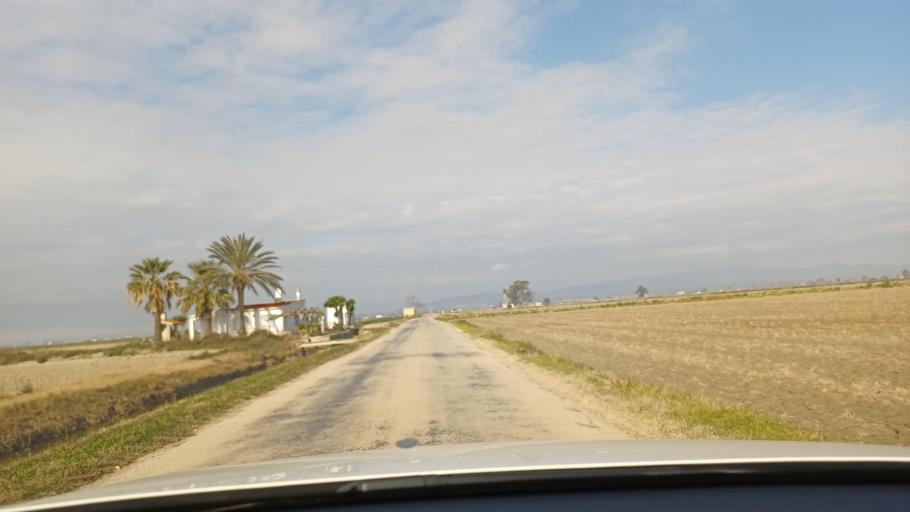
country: ES
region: Catalonia
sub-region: Provincia de Tarragona
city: Deltebre
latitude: 40.6831
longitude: 0.6564
